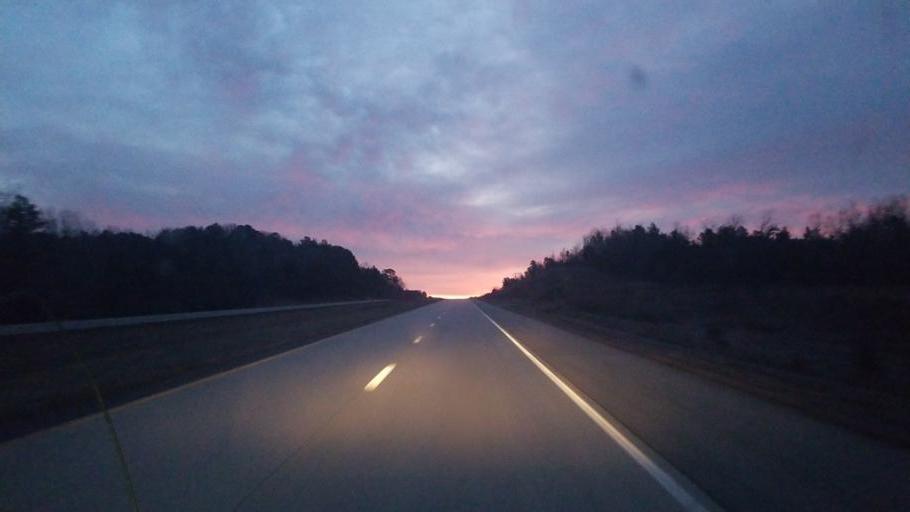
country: US
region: Missouri
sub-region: Shannon County
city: Winona
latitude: 36.9983
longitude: -91.4066
